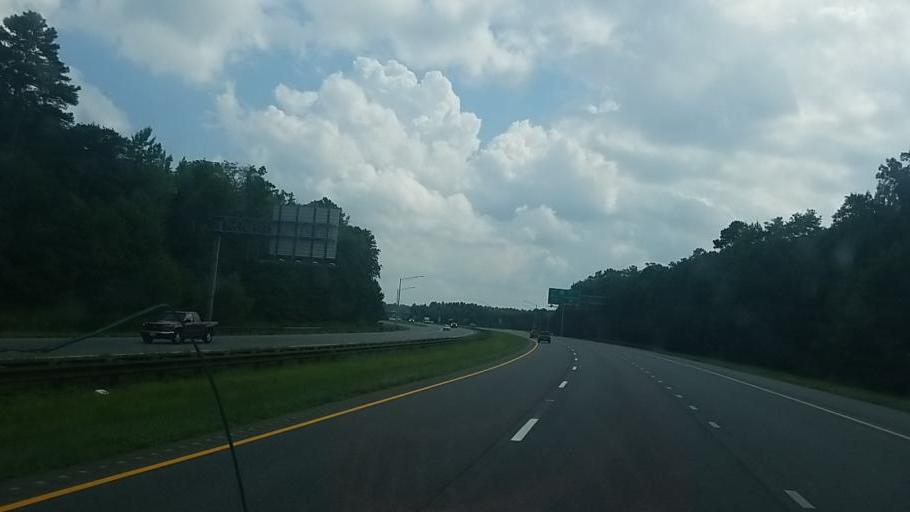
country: US
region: Maryland
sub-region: Worcester County
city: Ocean Pines
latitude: 38.3829
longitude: -75.2063
